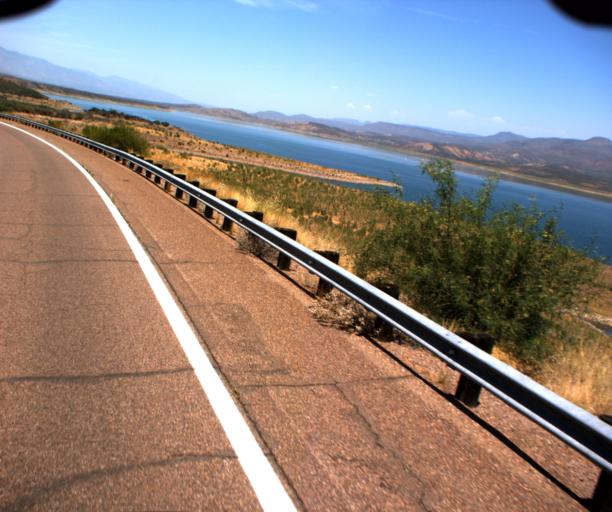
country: US
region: Arizona
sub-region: Gila County
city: Tonto Basin
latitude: 33.6936
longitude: -111.1764
